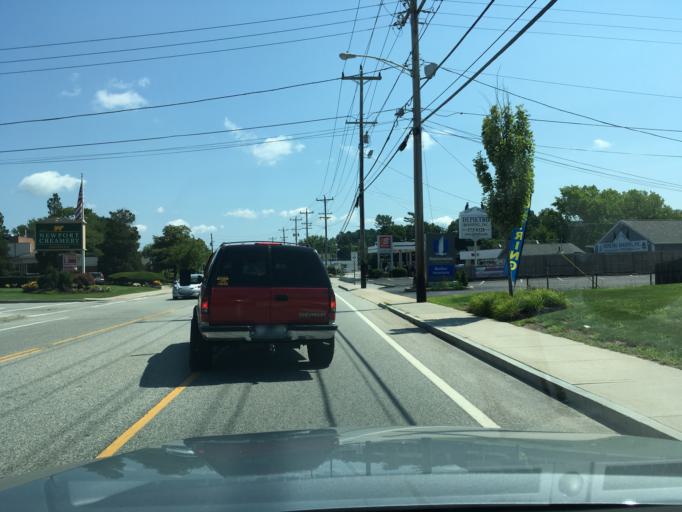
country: US
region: Rhode Island
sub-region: Kent County
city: West Warwick
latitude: 41.6818
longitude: -71.5638
